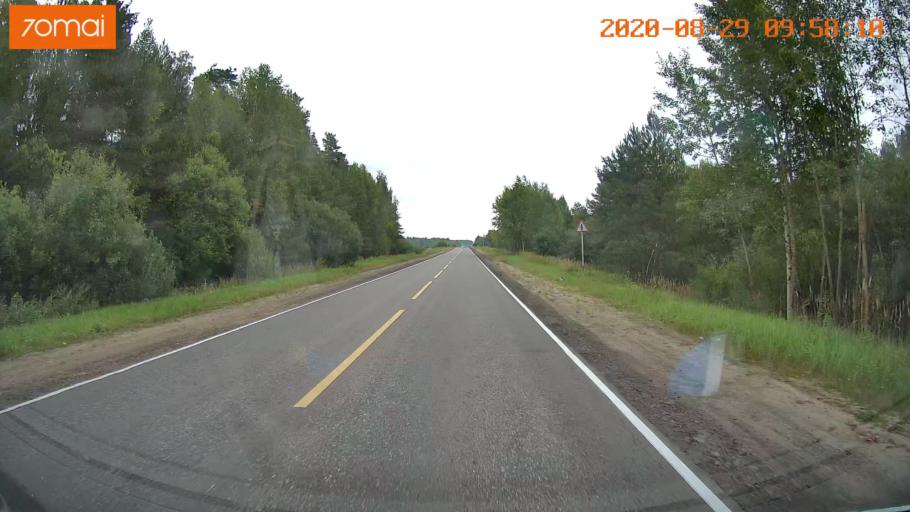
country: RU
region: Ivanovo
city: Zarechnyy
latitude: 57.4142
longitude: 42.3323
